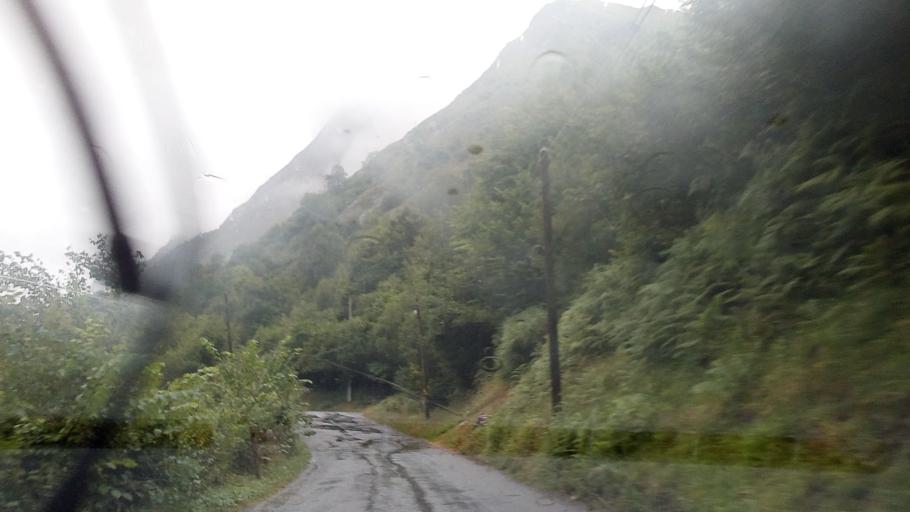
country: FR
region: Midi-Pyrenees
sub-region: Departement des Hautes-Pyrenees
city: Cauterets
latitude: 42.9455
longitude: -0.2262
